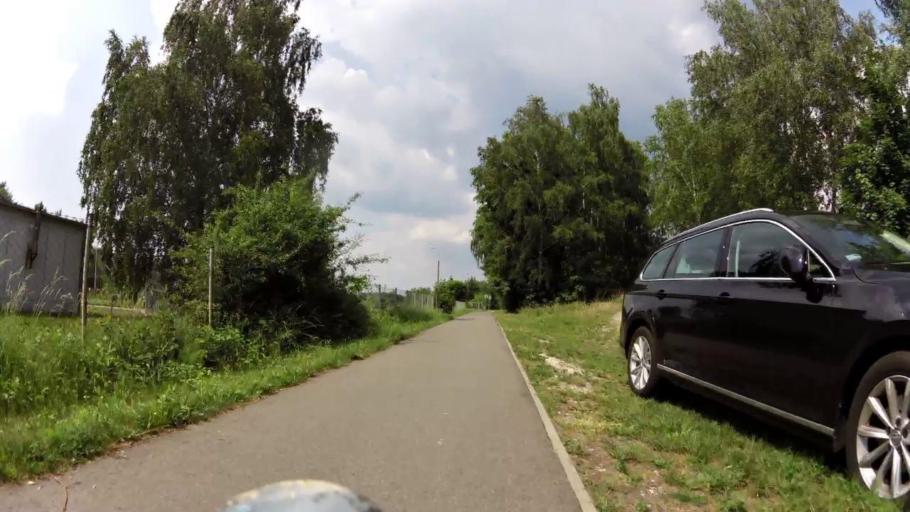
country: PL
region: Kujawsko-Pomorskie
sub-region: Powiat bydgoski
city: Koronowo
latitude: 53.3019
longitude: 17.9459
